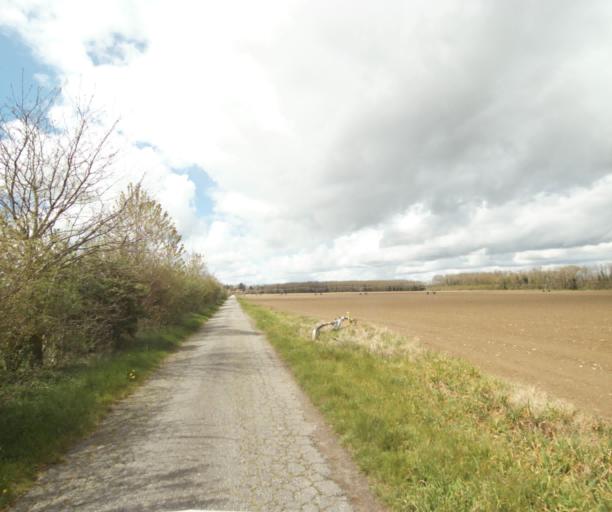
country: FR
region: Midi-Pyrenees
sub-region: Departement de la Haute-Garonne
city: Calmont
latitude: 43.2541
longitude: 1.6345
